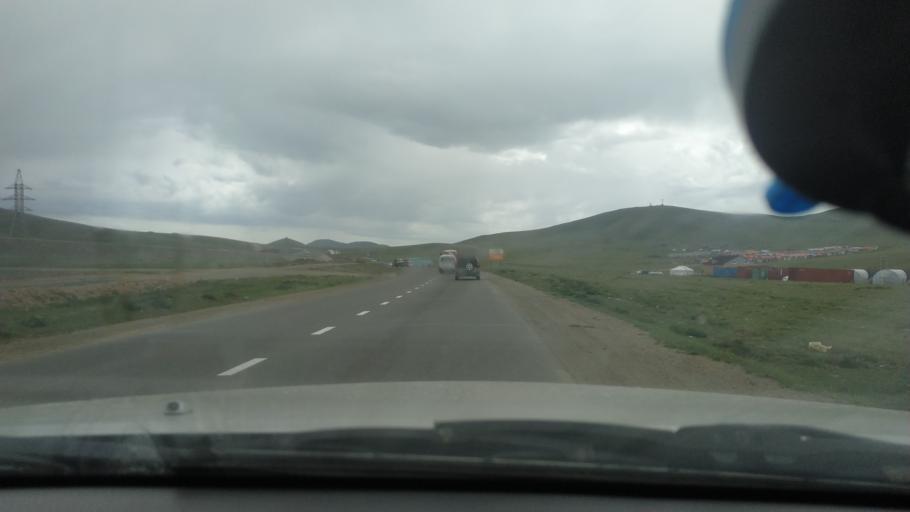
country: MN
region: Ulaanbaatar
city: Ulaanbaatar
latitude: 47.8010
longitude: 106.7468
